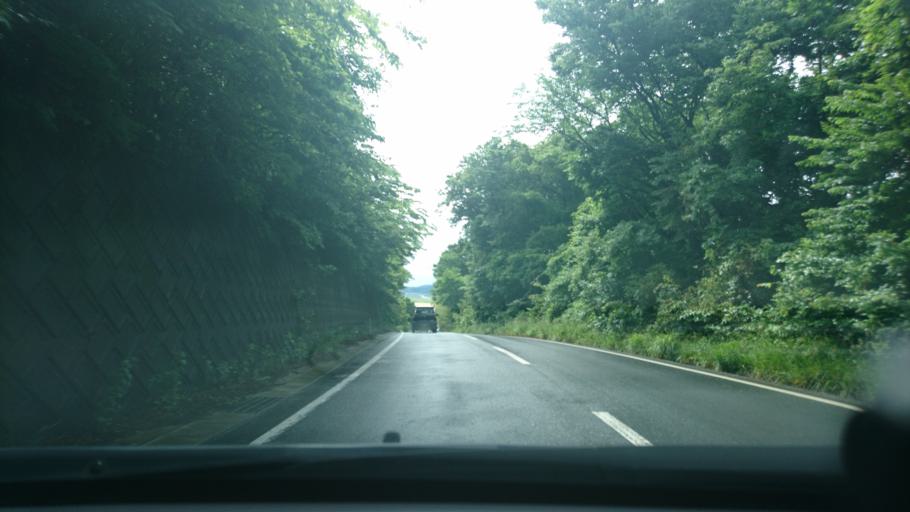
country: JP
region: Miyagi
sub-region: Oshika Gun
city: Onagawa Cho
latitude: 38.4421
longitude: 141.3811
